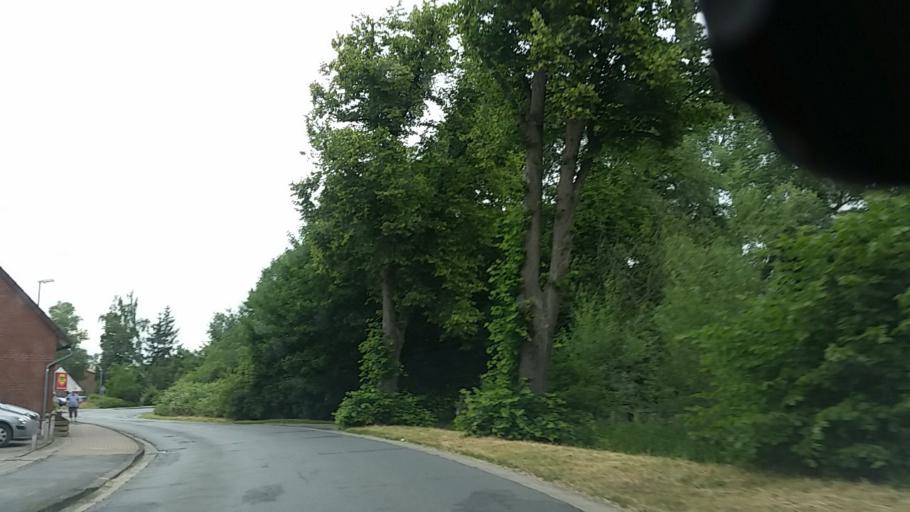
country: DE
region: Lower Saxony
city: Lehre
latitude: 52.3526
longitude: 10.7098
